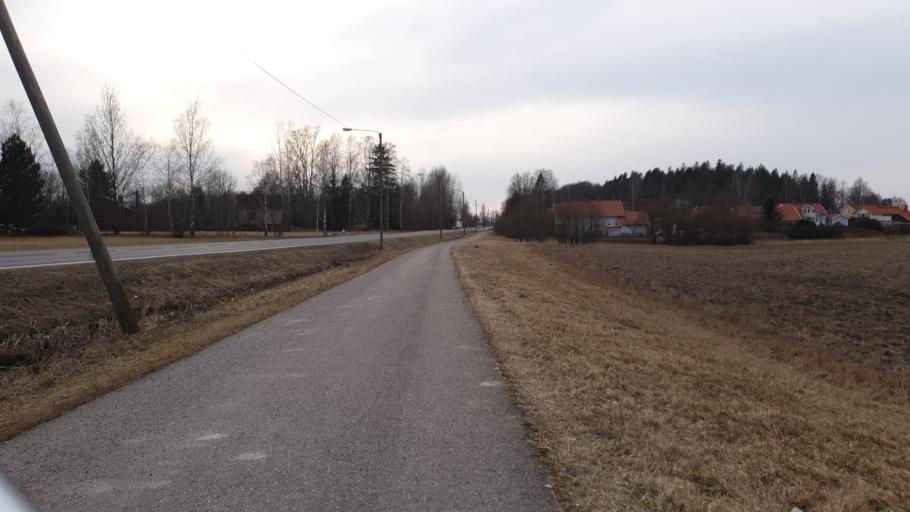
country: FI
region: Uusimaa
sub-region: Helsinki
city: Nurmijaervi
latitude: 60.3477
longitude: 24.8837
